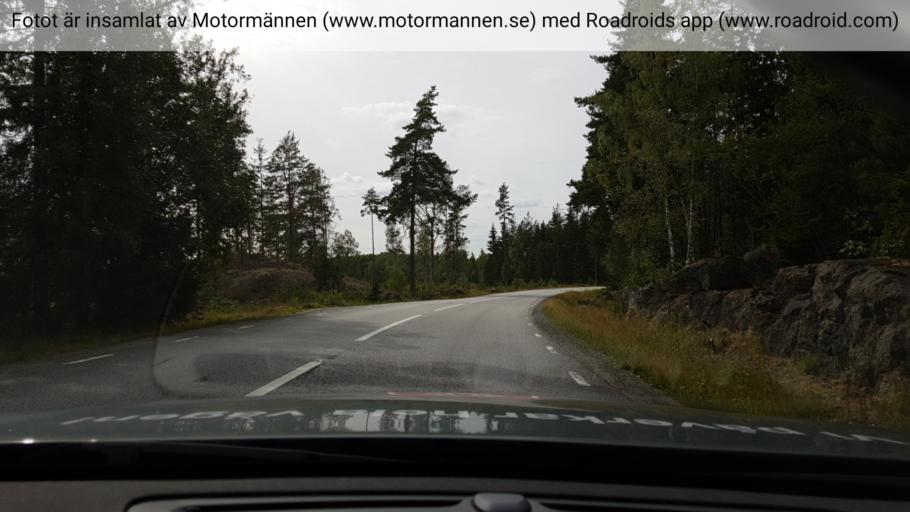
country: SE
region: Stockholm
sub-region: Botkyrka Kommun
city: Tullinge
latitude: 59.1234
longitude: 17.8858
